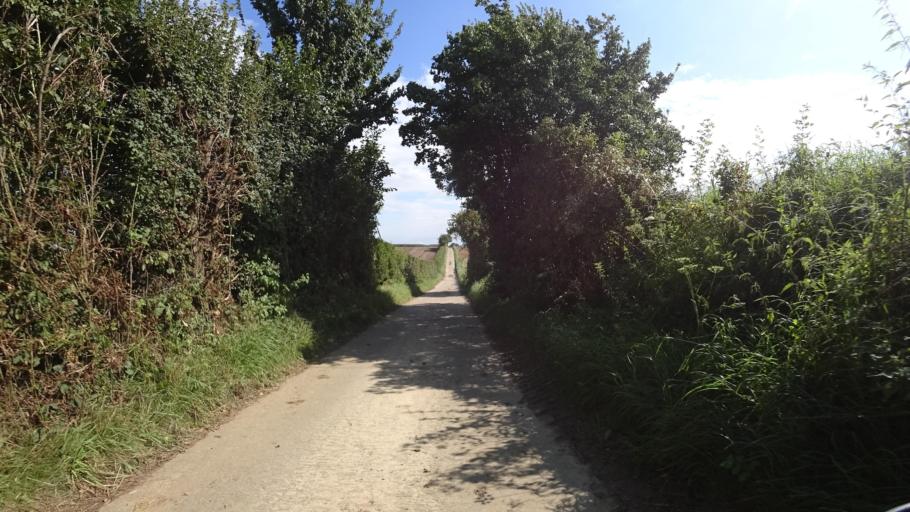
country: BE
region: Wallonia
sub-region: Province du Brabant Wallon
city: Louvain-la-Neuve
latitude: 50.6557
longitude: 4.6448
